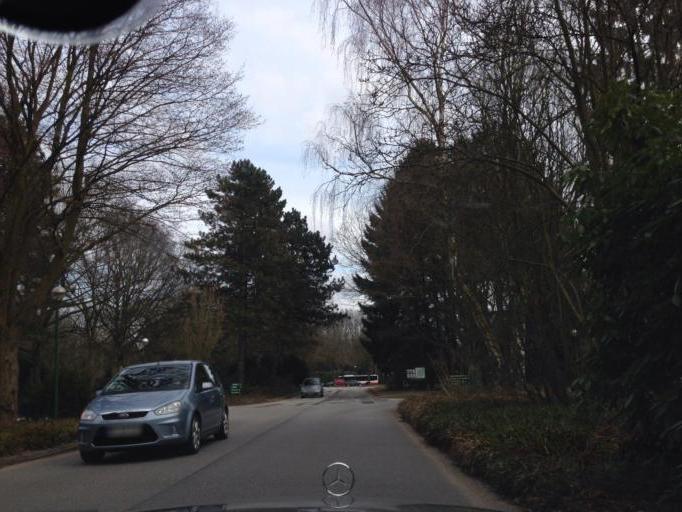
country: DE
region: Hamburg
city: Wandsbek
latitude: 53.5575
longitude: 10.1237
